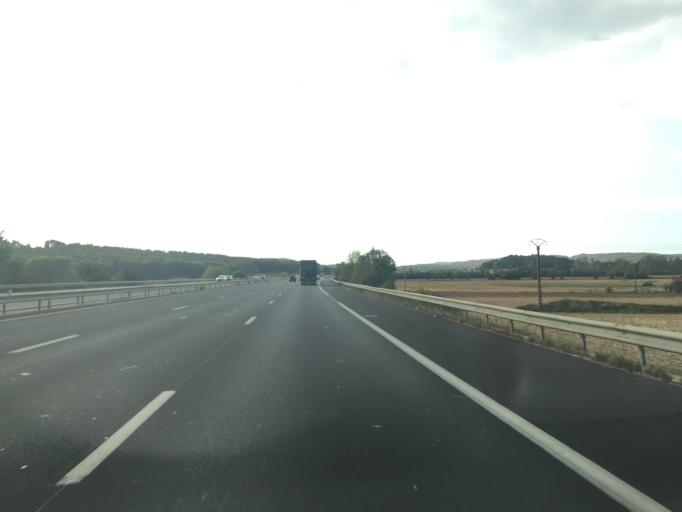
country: FR
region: Provence-Alpes-Cote d'Azur
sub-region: Departement des Bouches-du-Rhone
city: Eguilles
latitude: 43.5337
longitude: 5.3660
